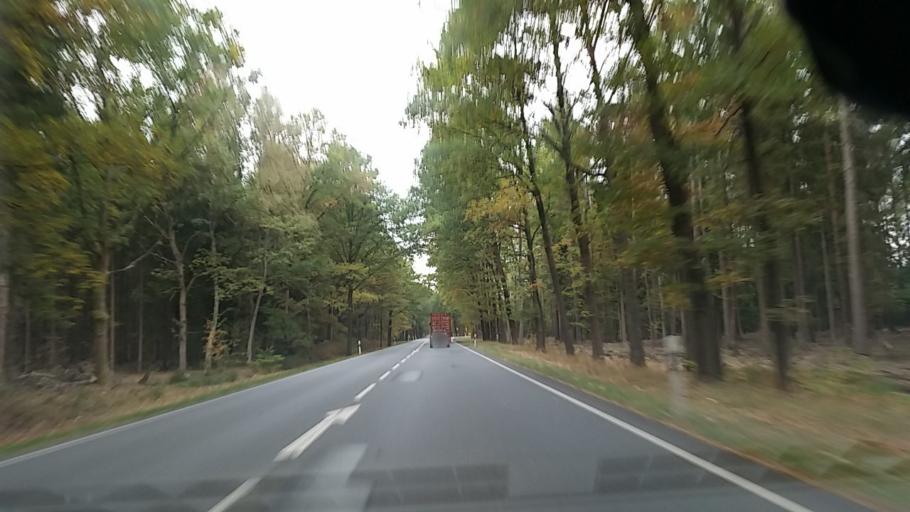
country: DE
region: Lower Saxony
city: Sprakensehl
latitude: 52.7845
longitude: 10.4911
